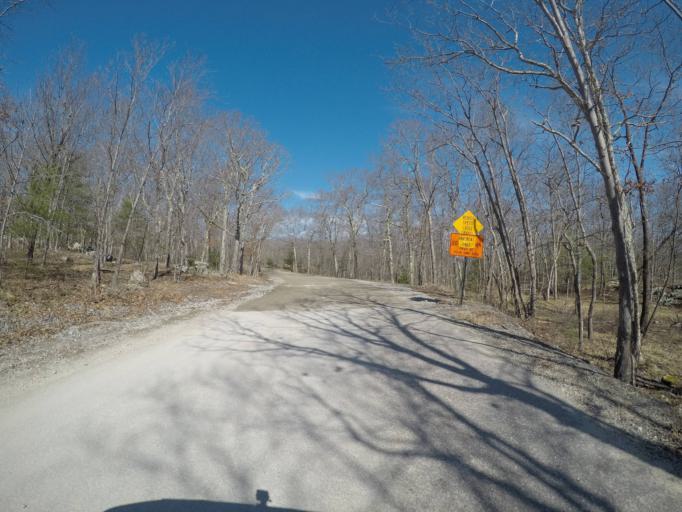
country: US
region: Massachusetts
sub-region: Norfolk County
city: Sharon
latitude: 42.0802
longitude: -71.1496
